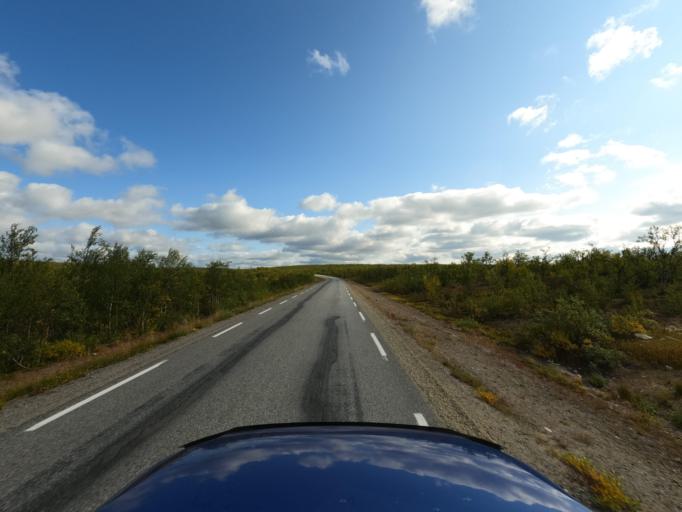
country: NO
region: Finnmark Fylke
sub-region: Porsanger
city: Lakselv
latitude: 69.3911
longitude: 24.5355
